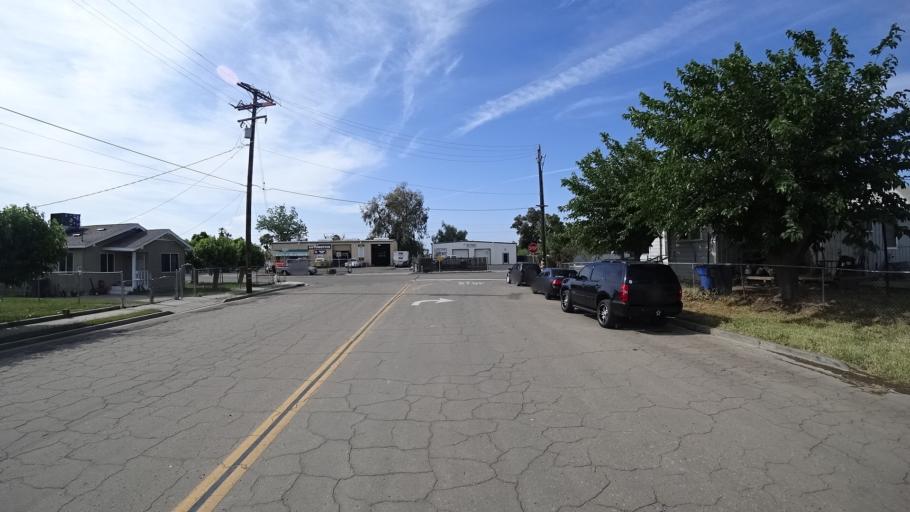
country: US
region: California
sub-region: Kings County
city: Hanford
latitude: 36.3242
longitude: -119.6435
